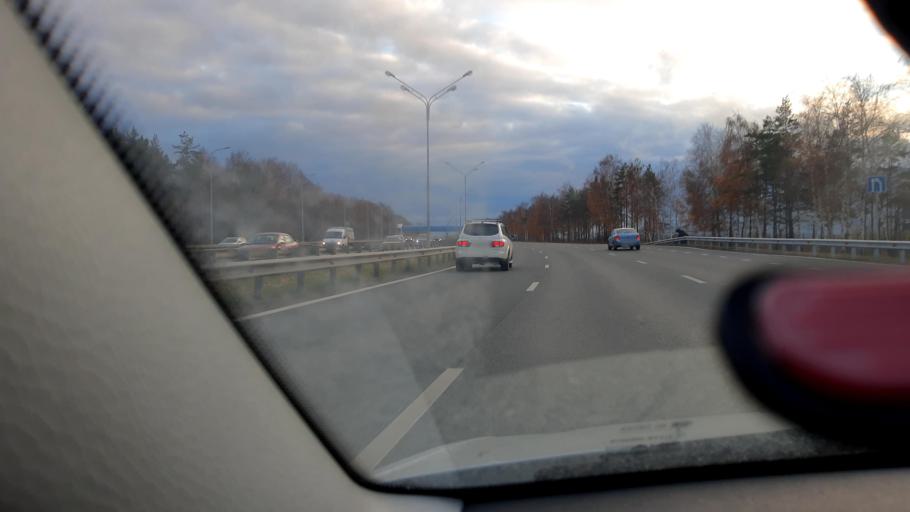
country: RU
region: Bashkortostan
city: Ufa
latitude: 54.6006
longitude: 55.9128
